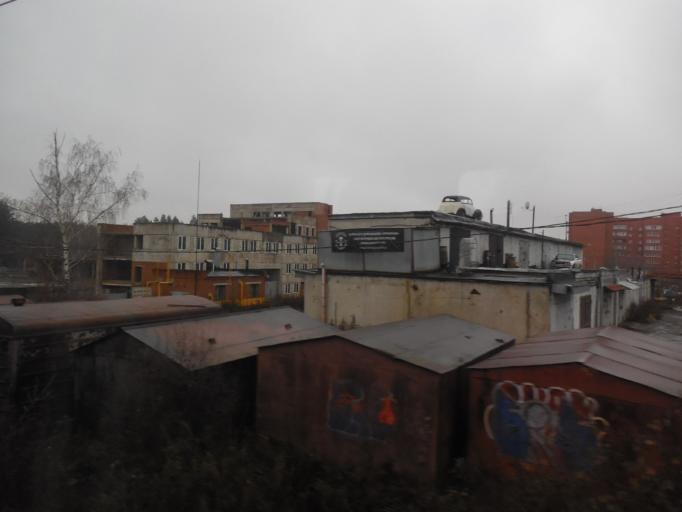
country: RU
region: Moskovskaya
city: Domodedovo
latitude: 55.4247
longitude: 37.7807
